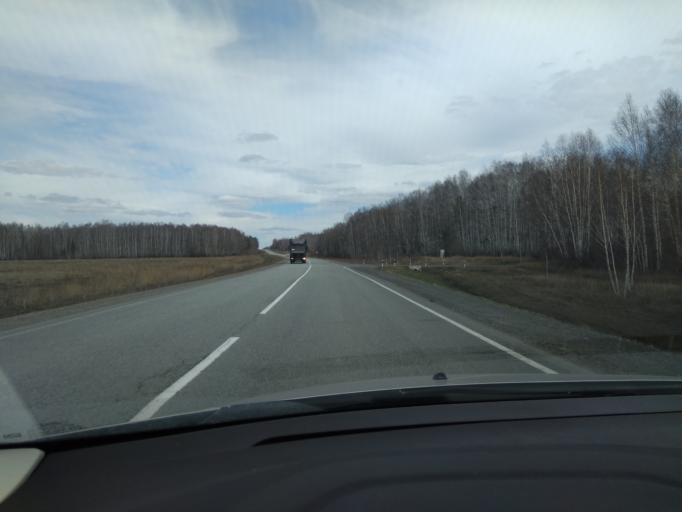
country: RU
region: Sverdlovsk
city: Yelanskiy
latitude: 56.7602
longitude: 62.3981
